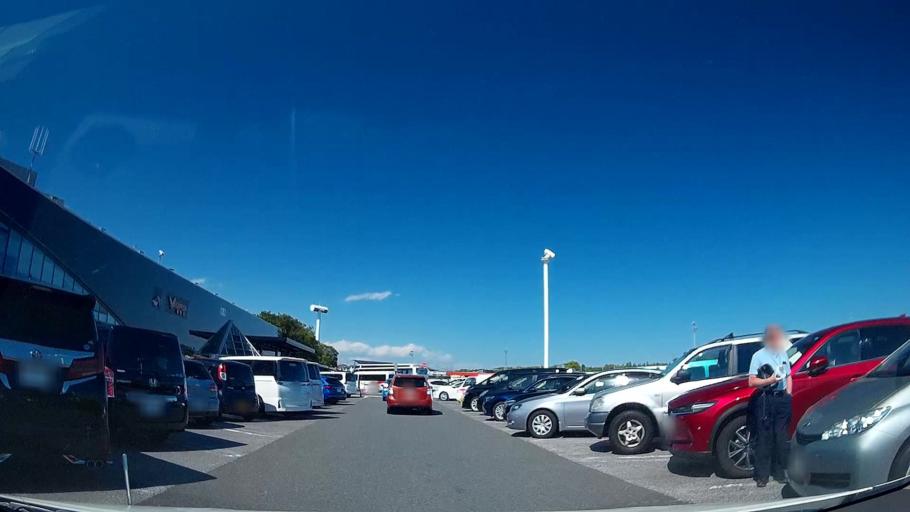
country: JP
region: Kanagawa
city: Atsugi
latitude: 35.4320
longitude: 139.3988
